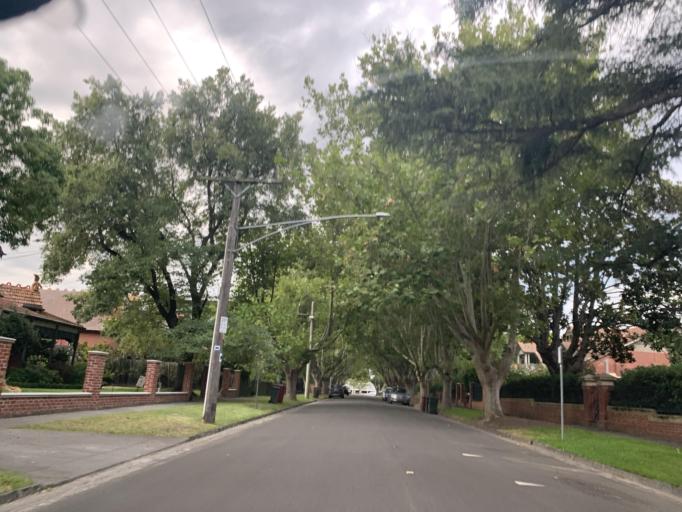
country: AU
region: Victoria
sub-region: Stonnington
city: Malvern East
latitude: -37.8738
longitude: 145.0440
